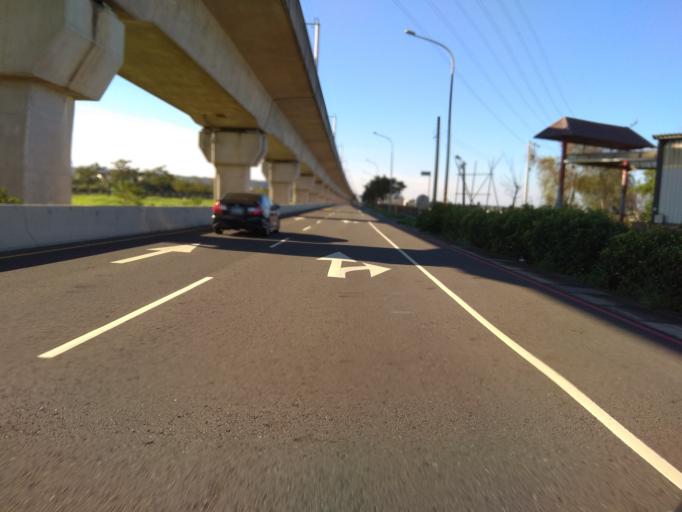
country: TW
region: Taiwan
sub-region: Hsinchu
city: Zhubei
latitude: 24.9058
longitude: 121.0851
